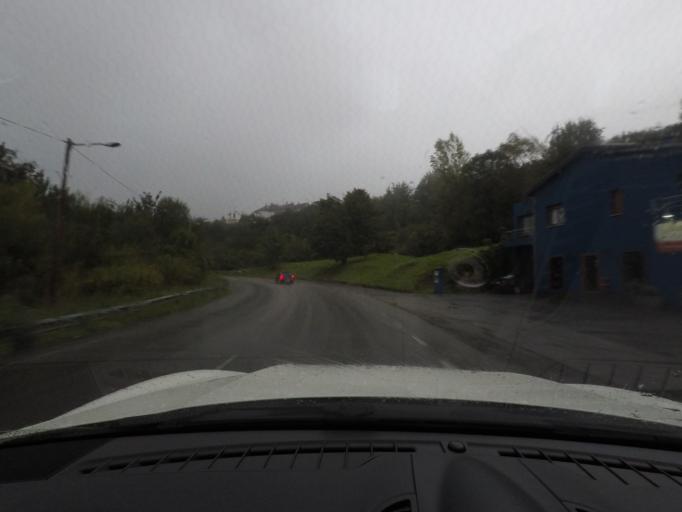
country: ES
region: Asturias
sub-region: Province of Asturias
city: Oviedo
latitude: 43.3531
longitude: -5.8775
